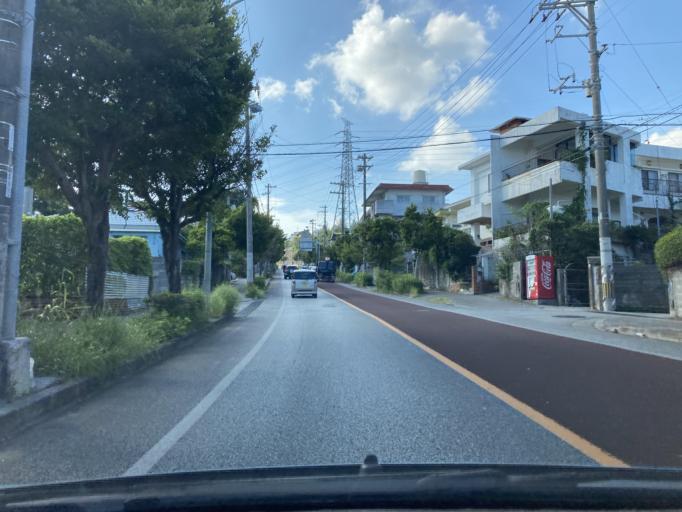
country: JP
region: Okinawa
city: Okinawa
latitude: 26.3259
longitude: 127.8217
